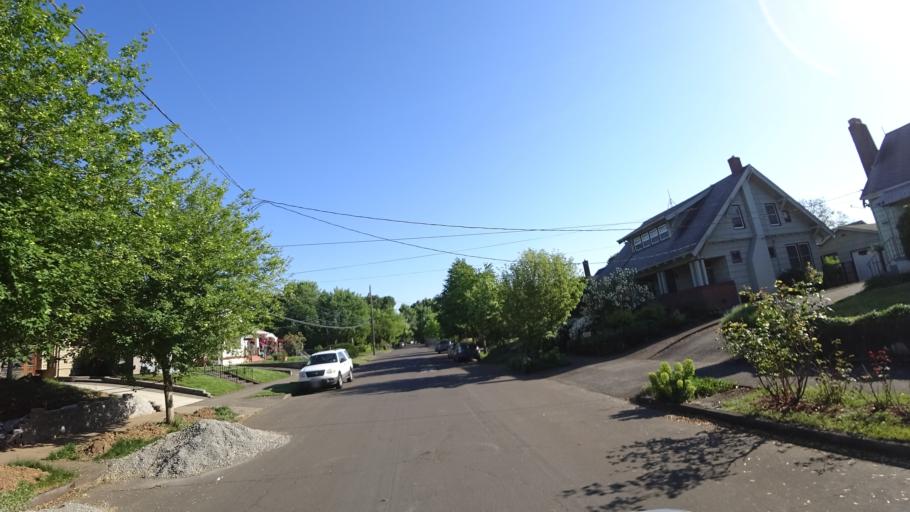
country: US
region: Oregon
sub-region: Multnomah County
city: Portland
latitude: 45.5540
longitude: -122.6851
